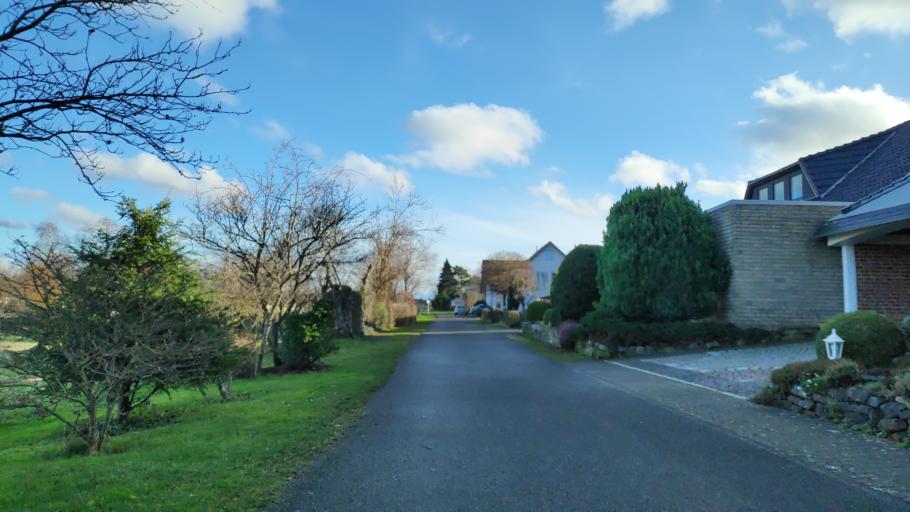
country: DE
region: North Rhine-Westphalia
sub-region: Regierungsbezirk Detmold
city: Minden
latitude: 52.2745
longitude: 8.8759
